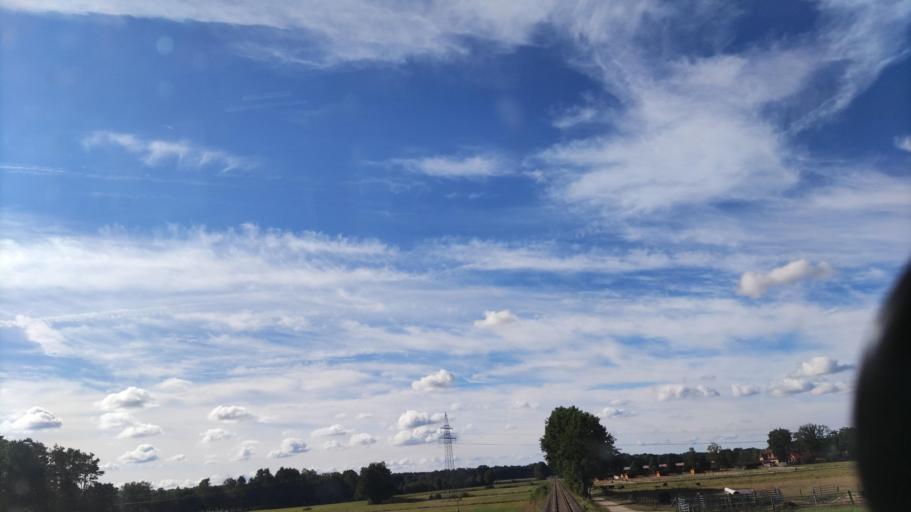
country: DE
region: Lower Saxony
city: Soltau
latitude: 53.0013
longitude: 9.8881
